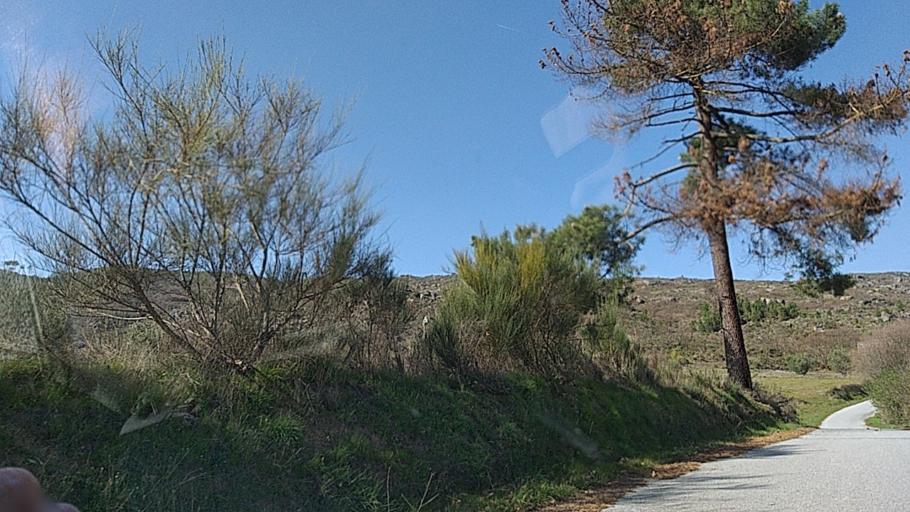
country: PT
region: Guarda
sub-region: Celorico da Beira
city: Celorico da Beira
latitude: 40.6451
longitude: -7.4284
